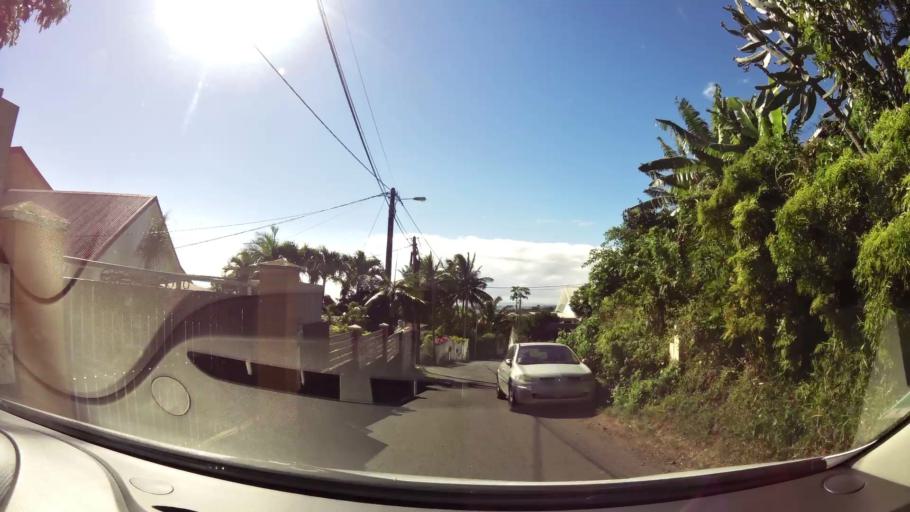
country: RE
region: Reunion
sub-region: Reunion
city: Saint-Denis
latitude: -20.9189
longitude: 55.4849
